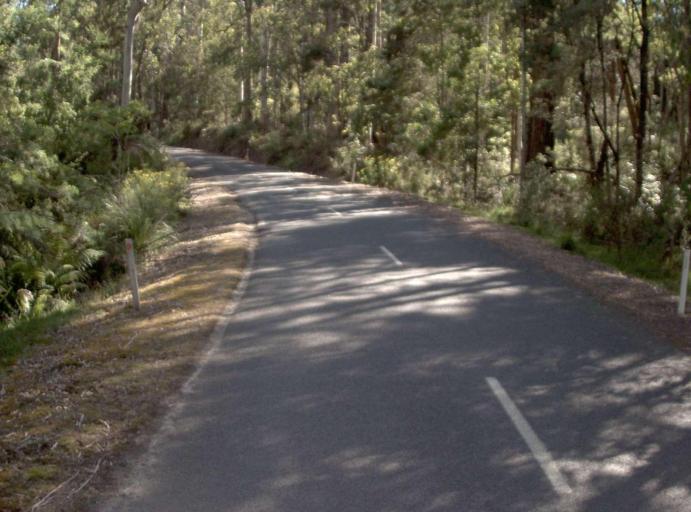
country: AU
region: Victoria
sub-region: East Gippsland
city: Lakes Entrance
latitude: -37.3959
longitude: 148.5941
